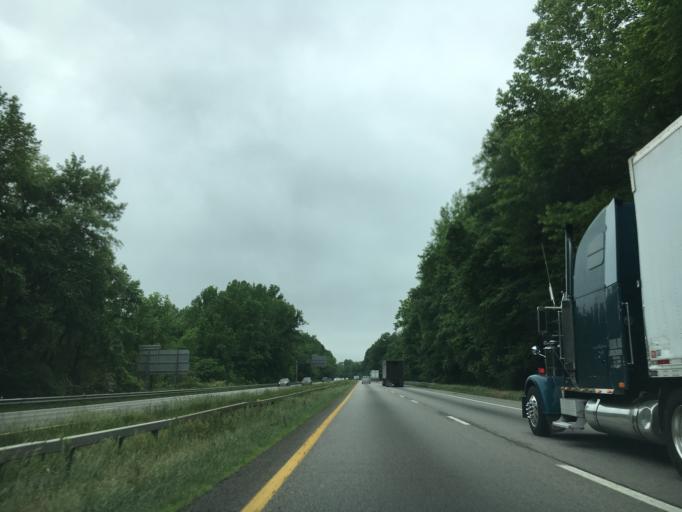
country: US
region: Virginia
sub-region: City of Petersburg
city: Petersburg
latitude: 37.2096
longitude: -77.4043
